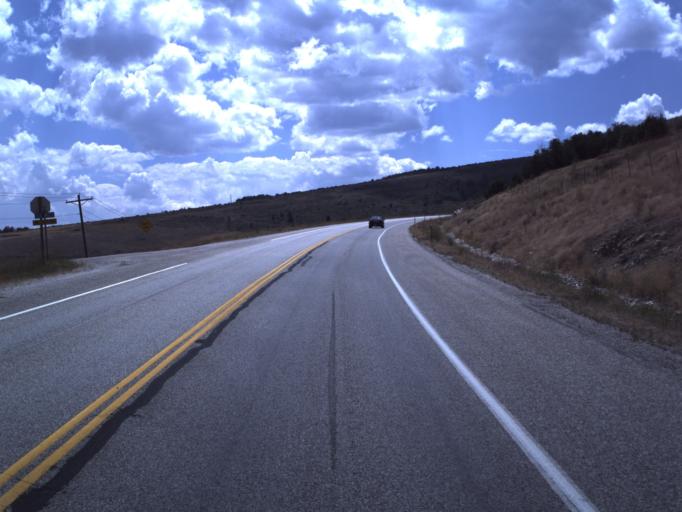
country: US
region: Idaho
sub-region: Bear Lake County
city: Paris
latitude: 41.9399
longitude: -111.4104
